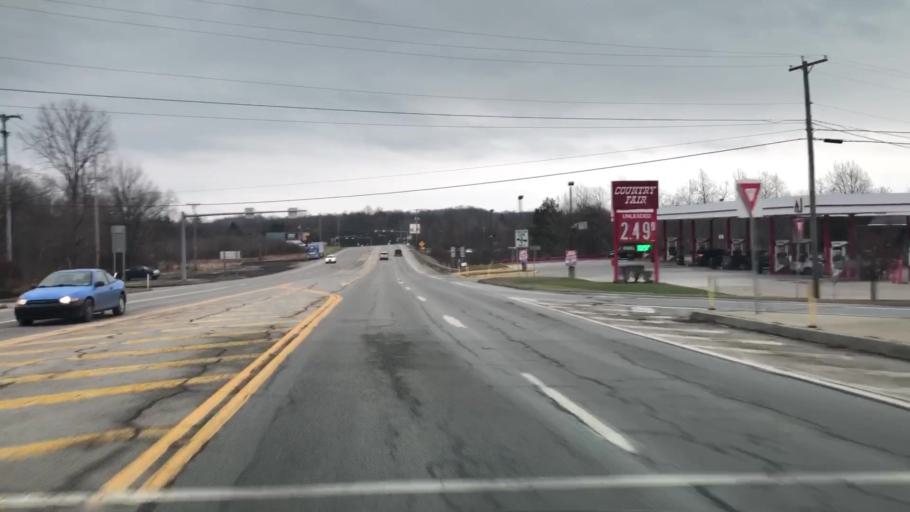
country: US
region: Pennsylvania
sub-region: Mercer County
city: Grove City
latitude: 41.1434
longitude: -80.1536
